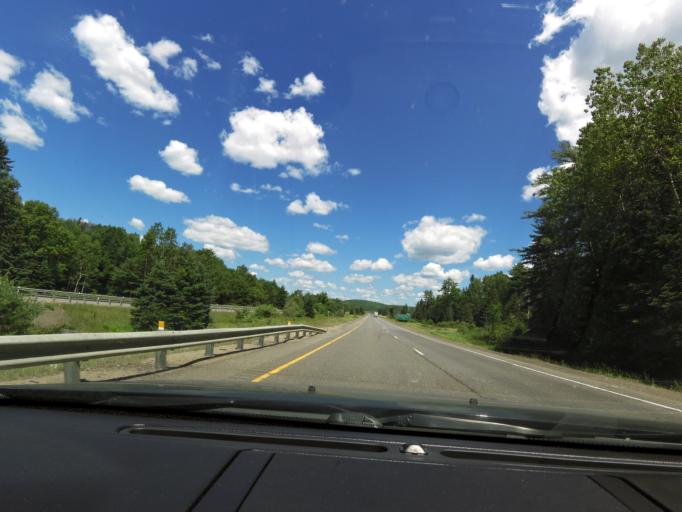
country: CA
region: Ontario
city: Huntsville
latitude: 45.3583
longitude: -79.2193
